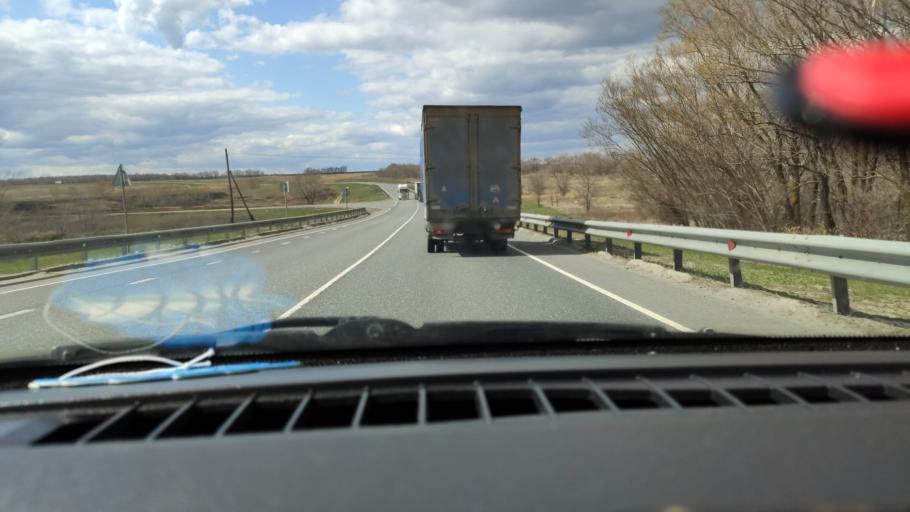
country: RU
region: Saratov
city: Balakovo
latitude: 52.1289
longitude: 47.7587
